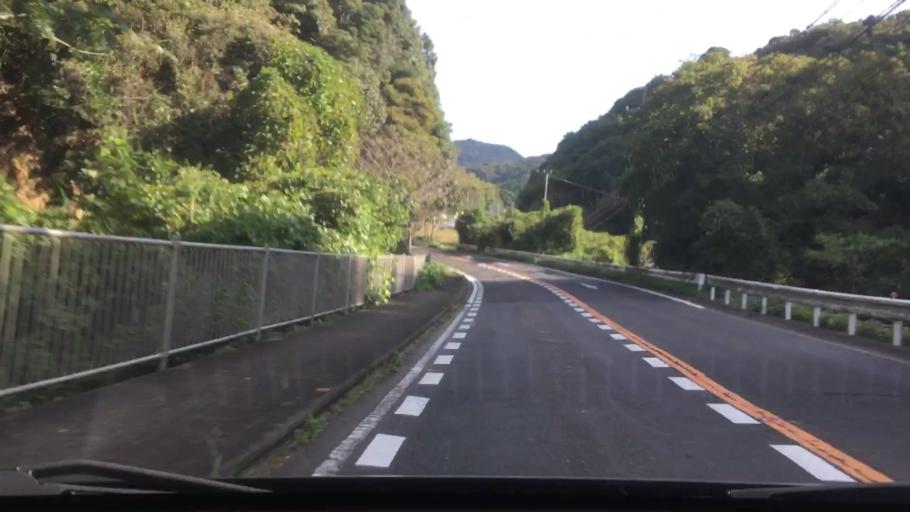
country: JP
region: Nagasaki
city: Sasebo
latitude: 33.1008
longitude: 129.7637
